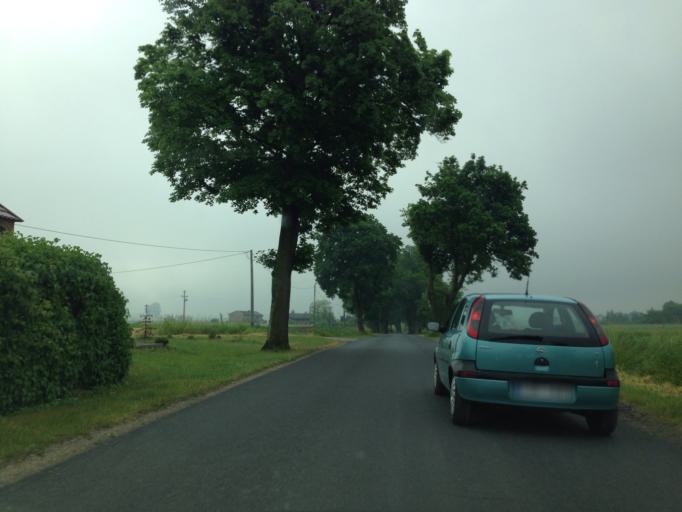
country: PL
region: Kujawsko-Pomorskie
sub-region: Powiat brodnicki
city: Brodnica
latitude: 53.3223
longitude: 19.3780
